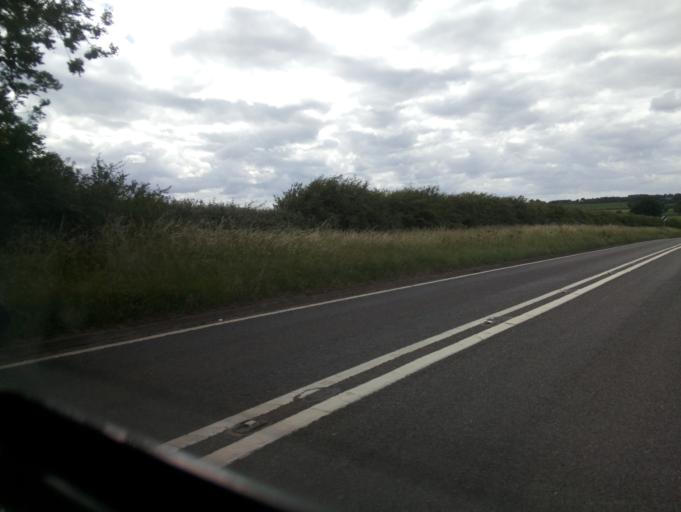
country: GB
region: England
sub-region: Leicestershire
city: Market Bosworth
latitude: 52.6187
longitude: -1.4769
